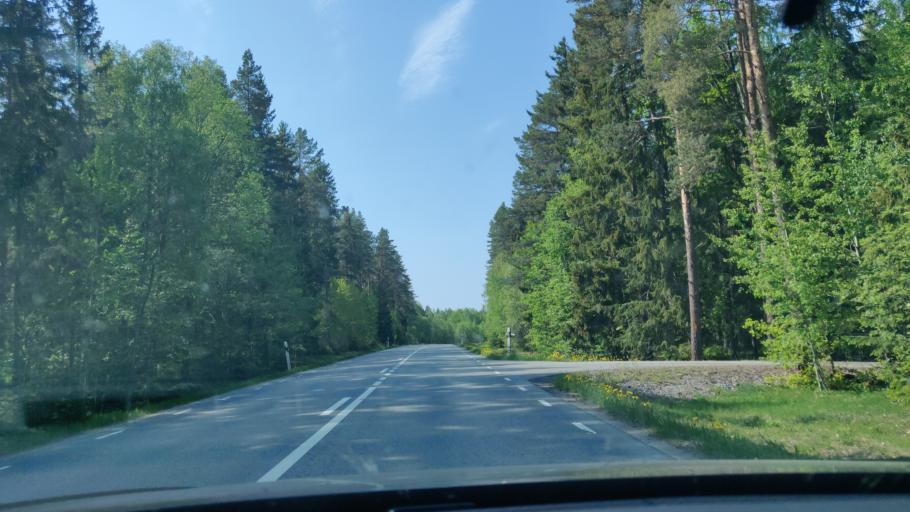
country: SE
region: Uppsala
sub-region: Heby Kommun
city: OEstervala
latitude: 60.1437
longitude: 17.2074
